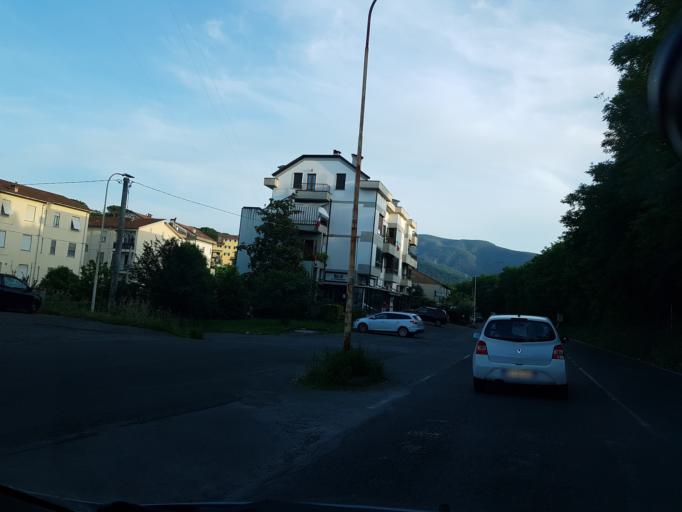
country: IT
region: Tuscany
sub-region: Provincia di Massa-Carrara
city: Terrarossa
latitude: 44.2195
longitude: 9.9690
